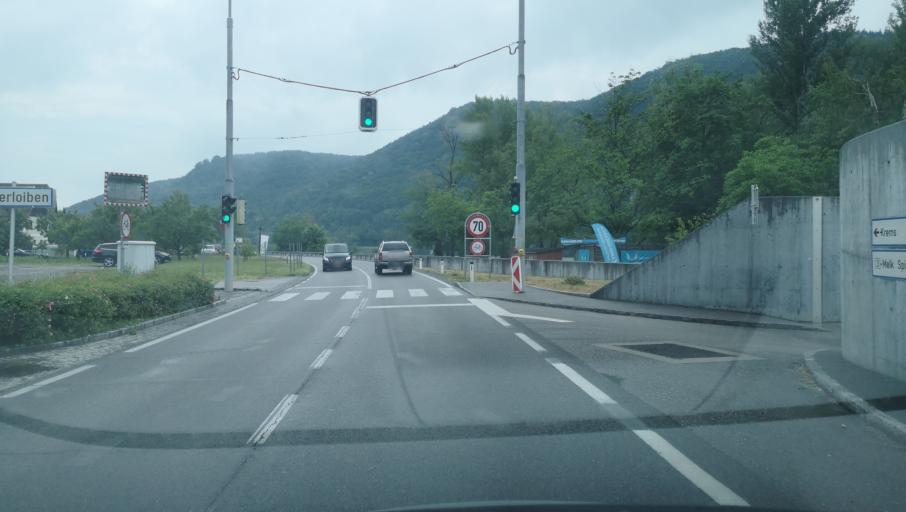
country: AT
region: Lower Austria
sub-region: Politischer Bezirk Krems
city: Durnstein
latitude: 48.3859
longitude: 15.5328
